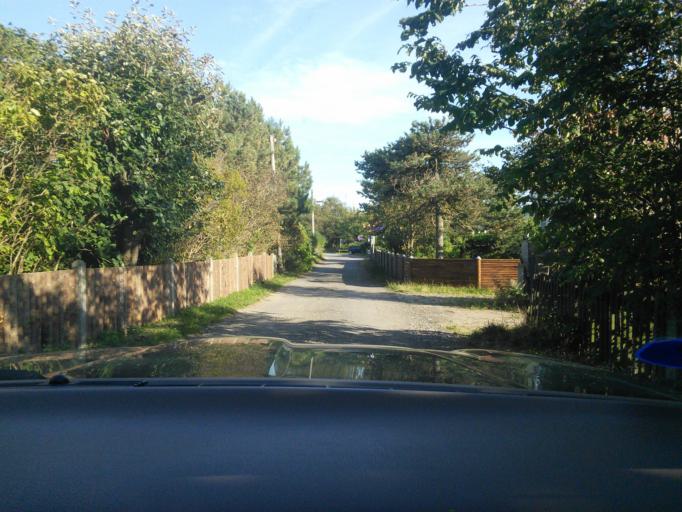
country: DK
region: Capital Region
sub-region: Halsnaes Kommune
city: Liseleje
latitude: 56.0133
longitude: 11.9624
